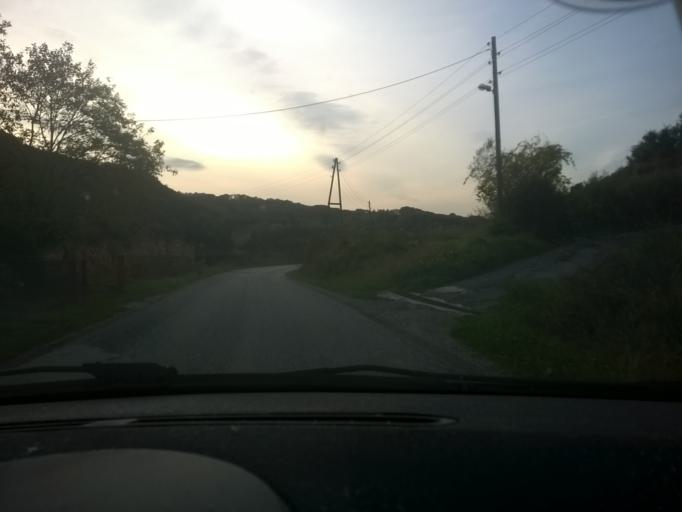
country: HR
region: Krapinsko-Zagorska
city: Zabok
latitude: 46.0854
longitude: 15.8908
